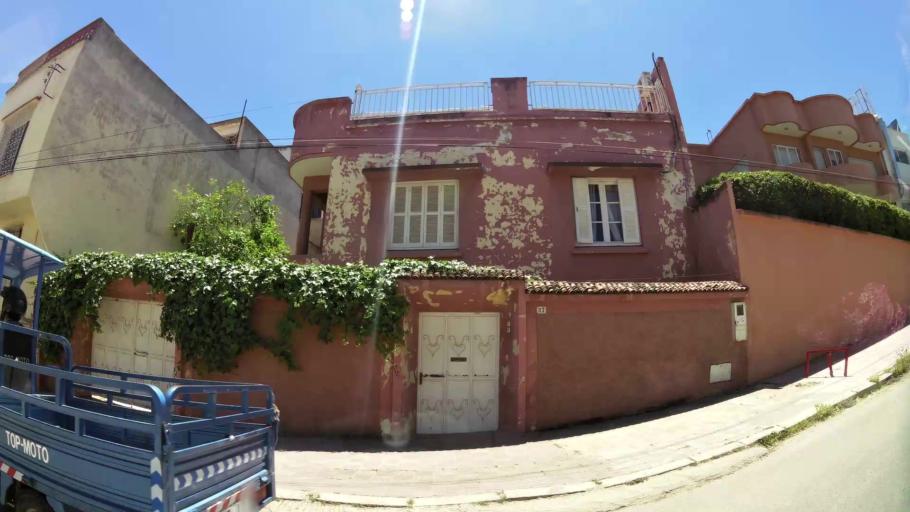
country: MA
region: Meknes-Tafilalet
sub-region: Meknes
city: Meknes
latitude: 33.9040
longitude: -5.5569
